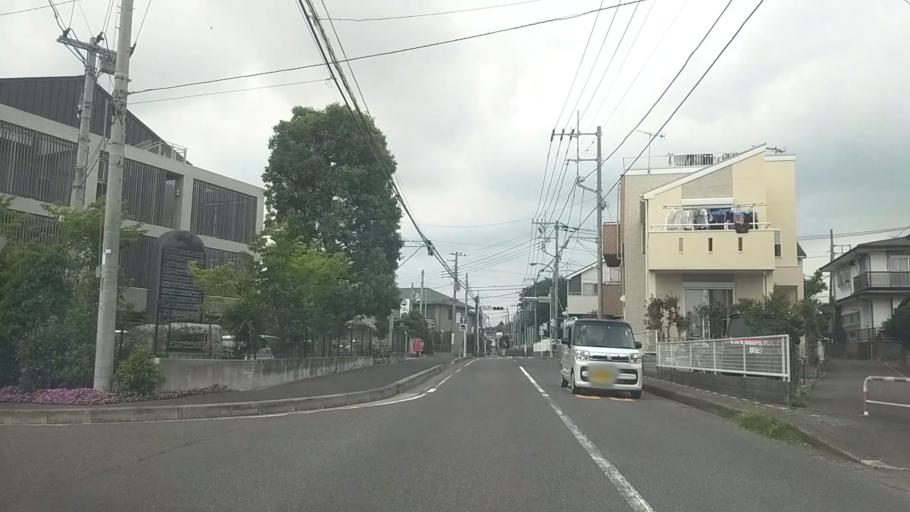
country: JP
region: Kanagawa
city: Atsugi
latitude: 35.4009
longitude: 139.4161
